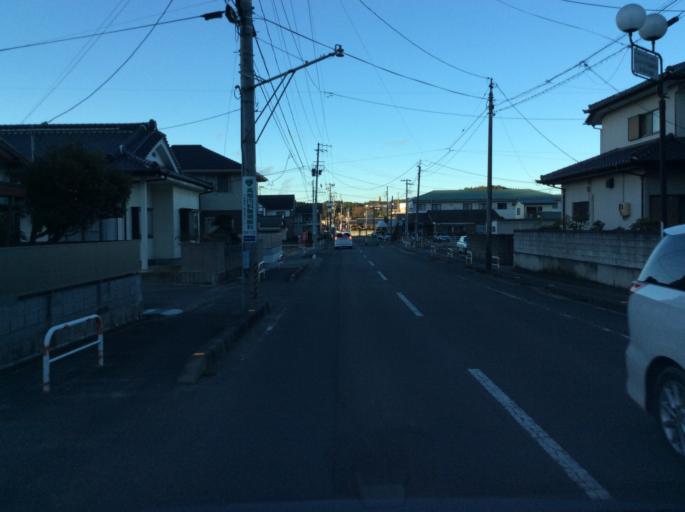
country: JP
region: Fukushima
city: Iwaki
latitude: 37.0576
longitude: 140.8676
